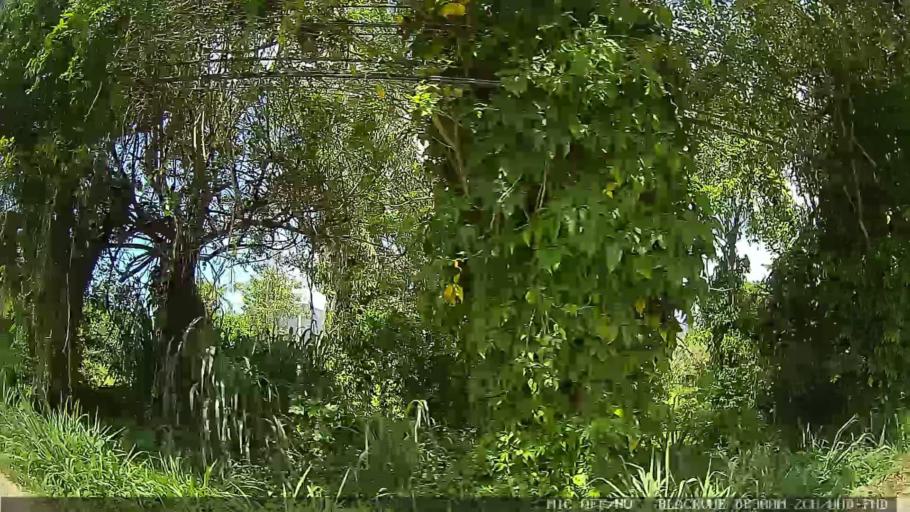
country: BR
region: Sao Paulo
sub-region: Peruibe
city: Peruibe
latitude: -24.3054
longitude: -47.0150
